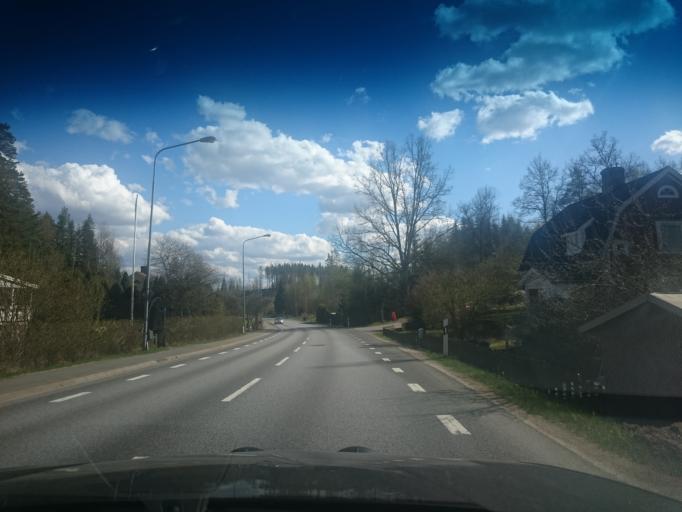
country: SE
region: Joenkoeping
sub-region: Vetlanda Kommun
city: Vetlanda
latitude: 57.2936
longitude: 15.1285
